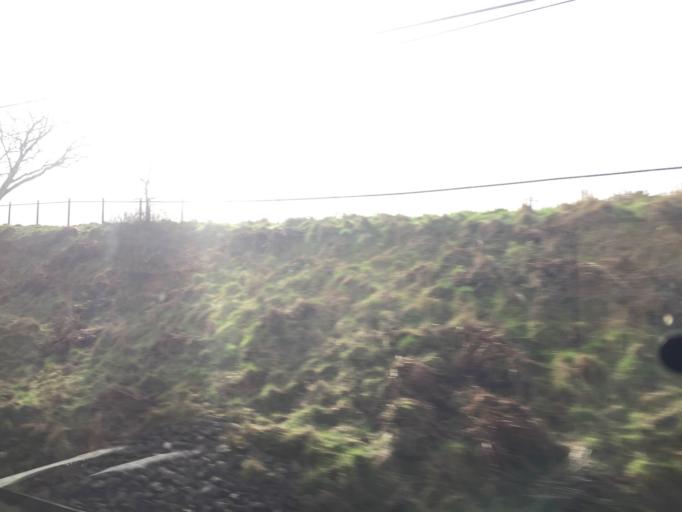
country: GB
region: England
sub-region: Cumbria
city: Kendal
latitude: 54.3548
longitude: -2.6822
